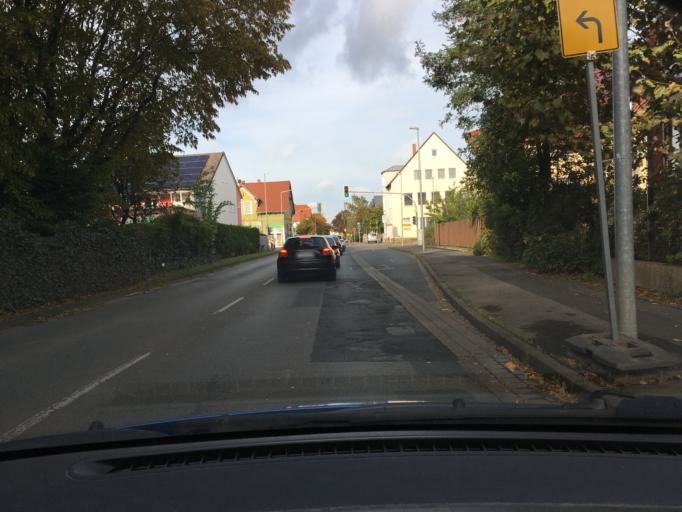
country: DE
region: Lower Saxony
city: Barsinghausen
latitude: 52.3037
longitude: 9.4671
